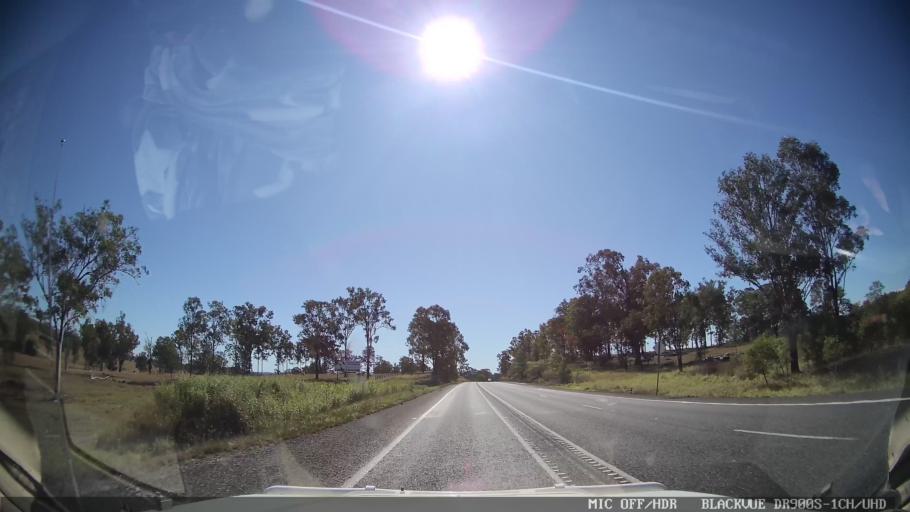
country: AU
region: Queensland
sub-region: Fraser Coast
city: Maryborough
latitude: -25.7740
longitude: 152.5965
